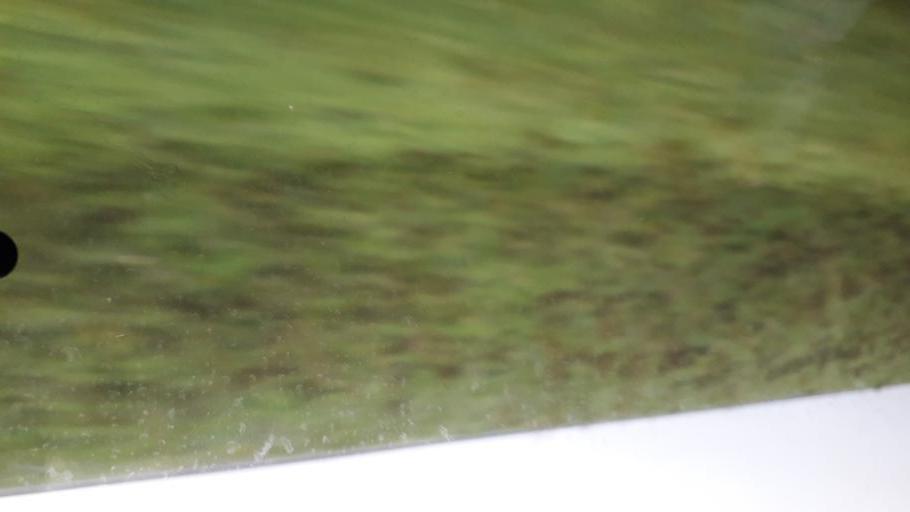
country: IE
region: Connaught
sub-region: County Galway
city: Athenry
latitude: 53.2933
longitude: -8.8085
